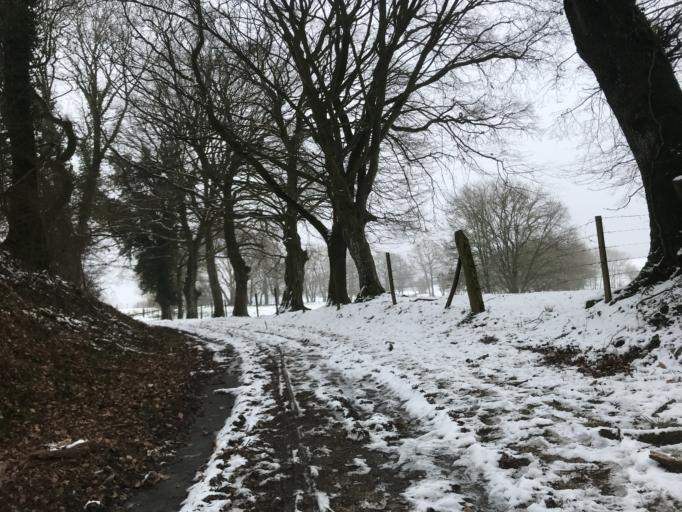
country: LU
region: Luxembourg
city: Belvaux
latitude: 49.4965
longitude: 5.9299
